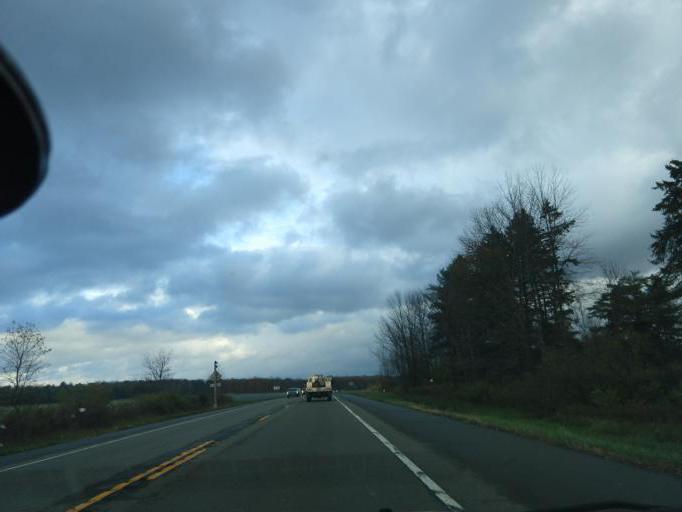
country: US
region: New York
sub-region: Tompkins County
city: Northeast Ithaca
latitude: 42.4829
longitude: -76.4524
